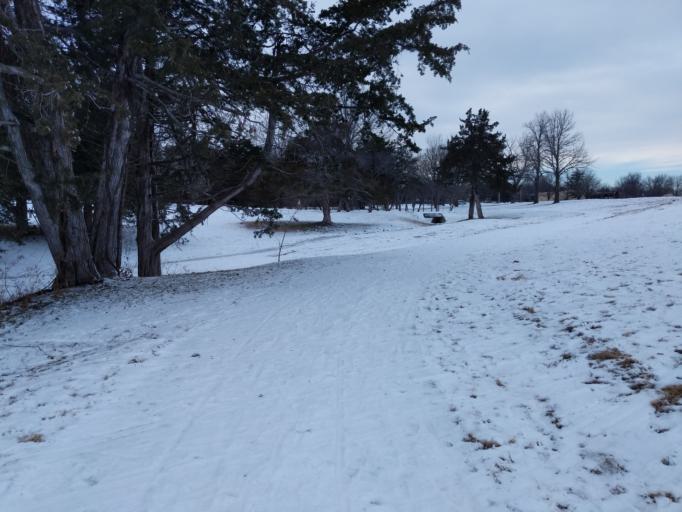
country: US
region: Kansas
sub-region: Riley County
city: Manhattan
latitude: 39.1968
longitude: -96.6200
